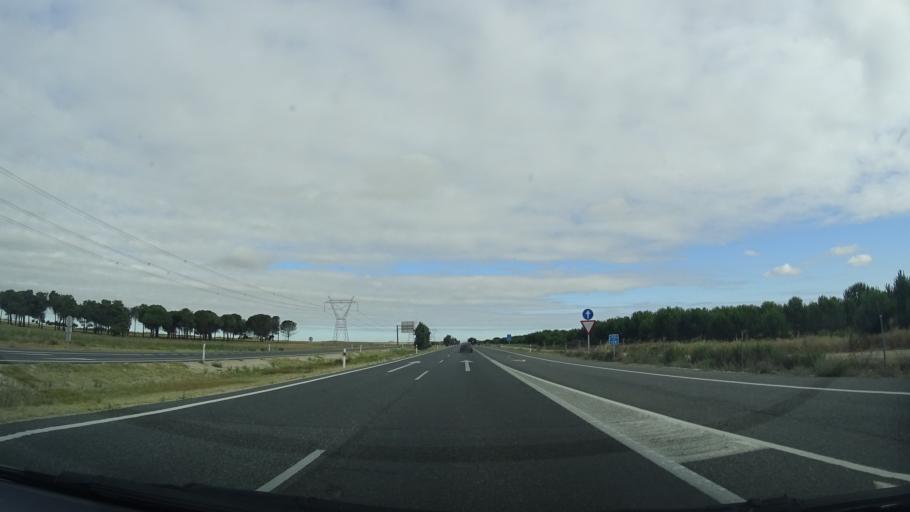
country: ES
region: Castille and Leon
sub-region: Provincia de Valladolid
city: San Pablo de la Moraleja
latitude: 41.1509
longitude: -4.7901
